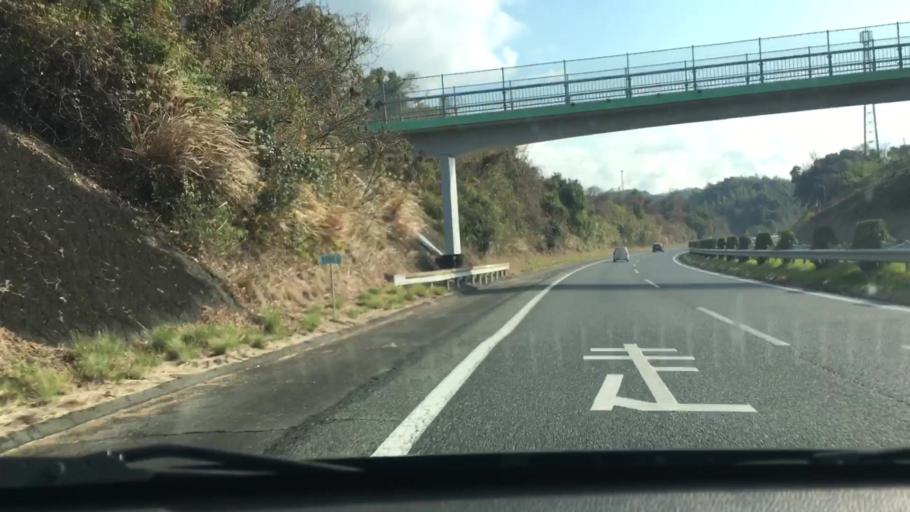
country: JP
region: Kumamoto
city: Matsubase
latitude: 32.6373
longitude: 130.7094
